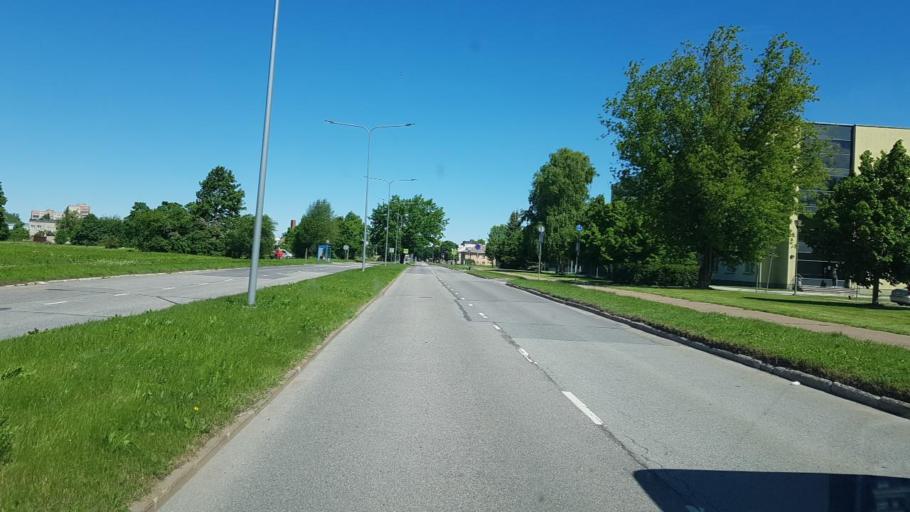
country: EE
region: Ida-Virumaa
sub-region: Narva linn
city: Narva
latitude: 59.3596
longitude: 28.1873
